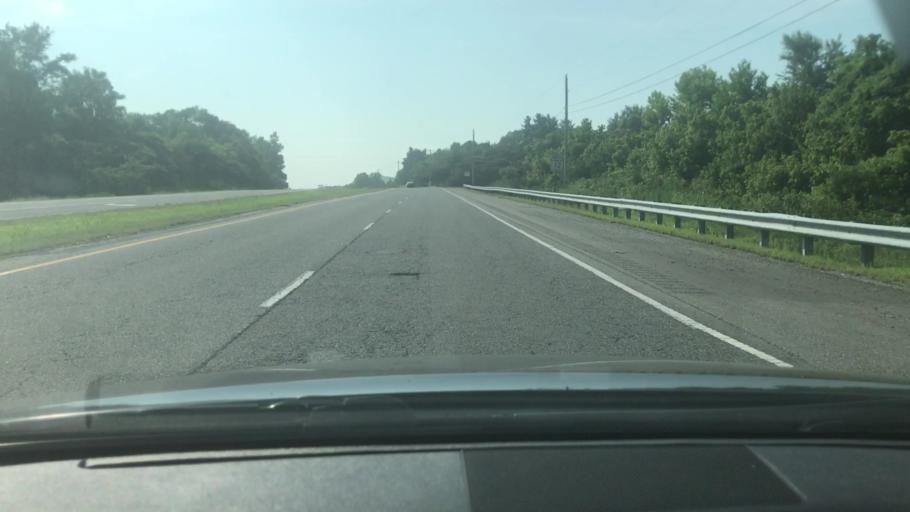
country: US
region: Tennessee
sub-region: Cheatham County
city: Ashland City
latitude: 36.2178
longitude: -86.9932
